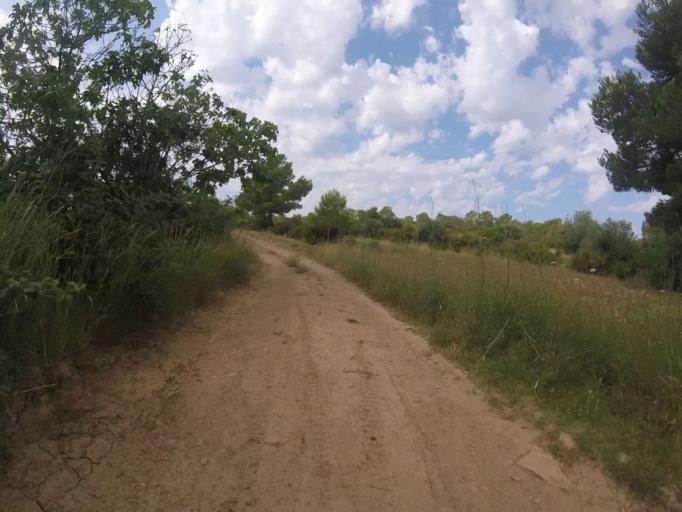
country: ES
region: Valencia
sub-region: Provincia de Castello
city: Alcala de Xivert
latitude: 40.3804
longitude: 0.2067
